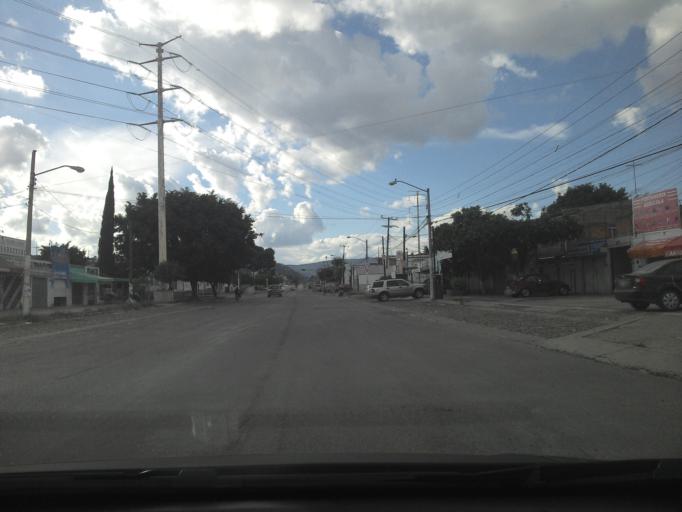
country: MX
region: Jalisco
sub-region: Tlajomulco de Zuniga
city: La Tijera
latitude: 20.6133
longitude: -103.4325
